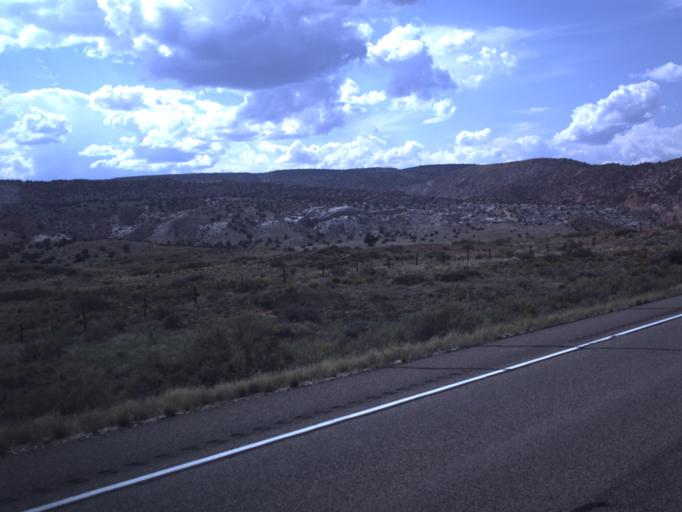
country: US
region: Arizona
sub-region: Coconino County
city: Page
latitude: 37.1214
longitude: -111.9442
